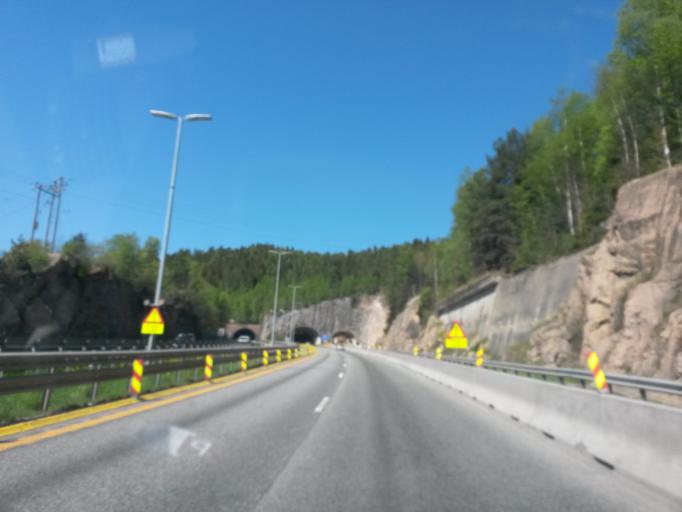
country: NO
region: Buskerud
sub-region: Lier
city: Tranby
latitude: 59.7890
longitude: 10.2730
